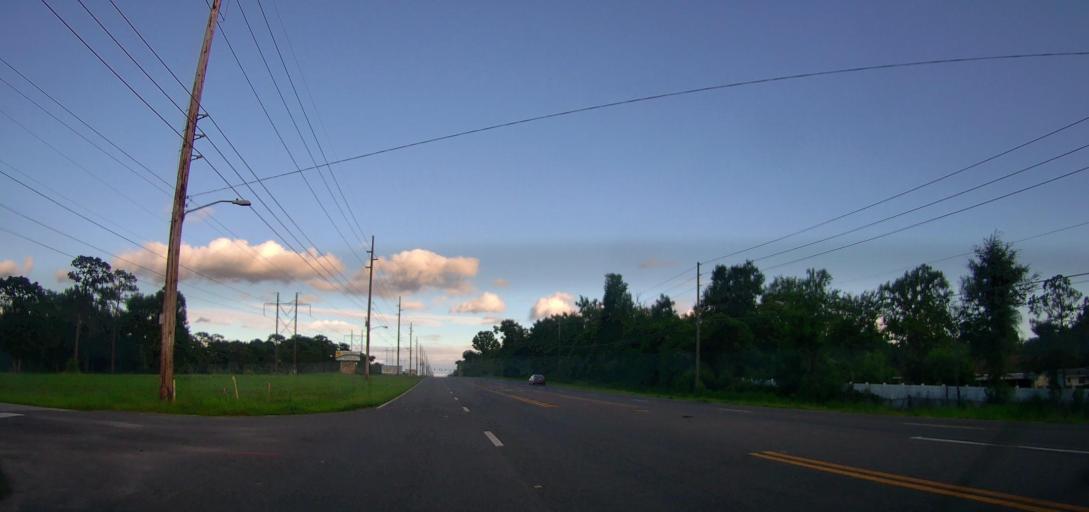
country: US
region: Florida
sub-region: Marion County
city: Silver Springs Shores
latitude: 29.1012
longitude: -82.0092
